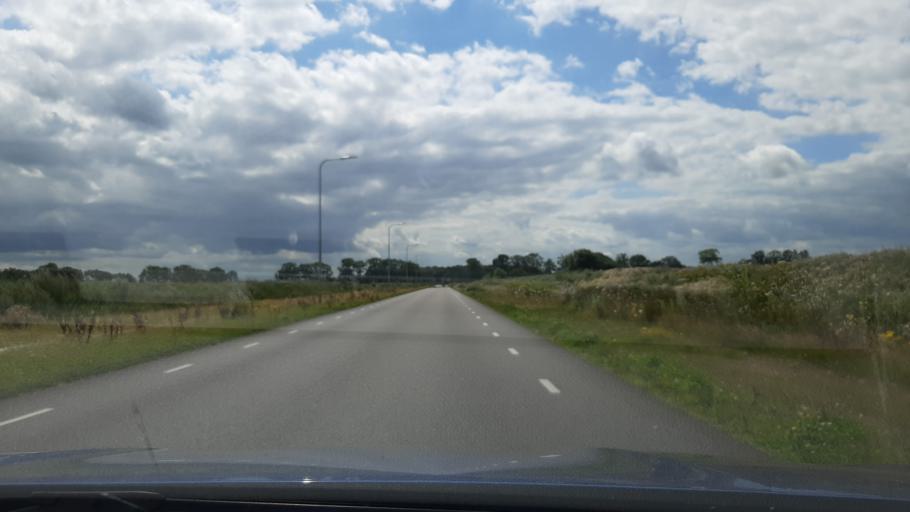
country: NL
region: Drenthe
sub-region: Gemeente Hoogeveen
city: Hoogeveen
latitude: 52.7059
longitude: 6.5169
